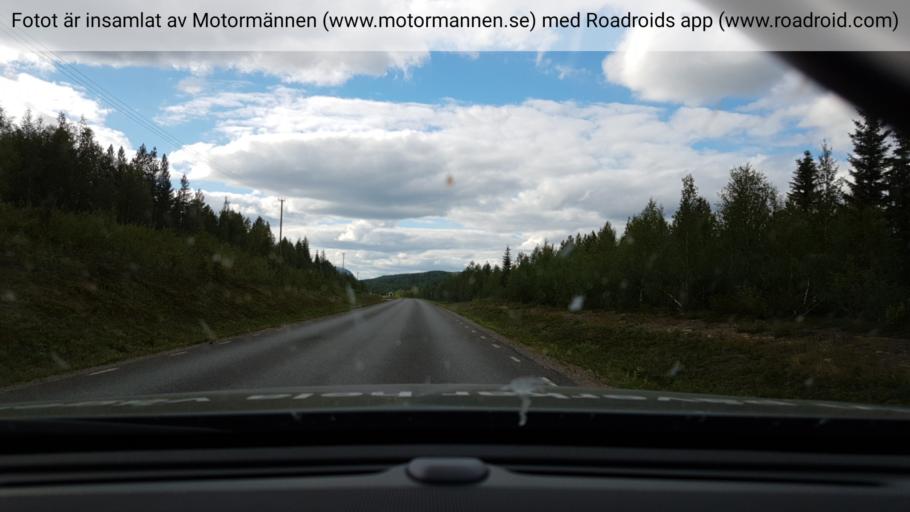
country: SE
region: Norrbotten
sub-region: Arjeplogs Kommun
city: Arjeplog
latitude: 66.2940
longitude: 17.1749
